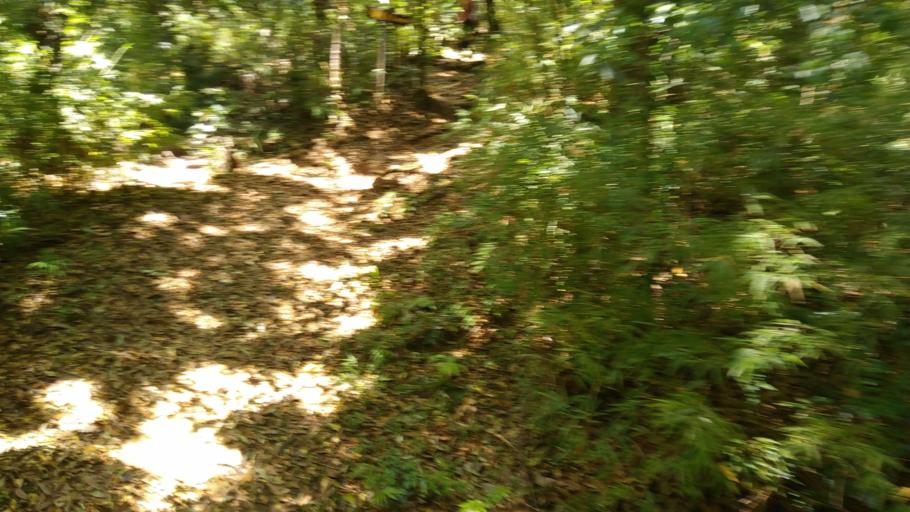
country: CR
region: Alajuela
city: Sabanilla
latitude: 10.1507
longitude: -84.2446
